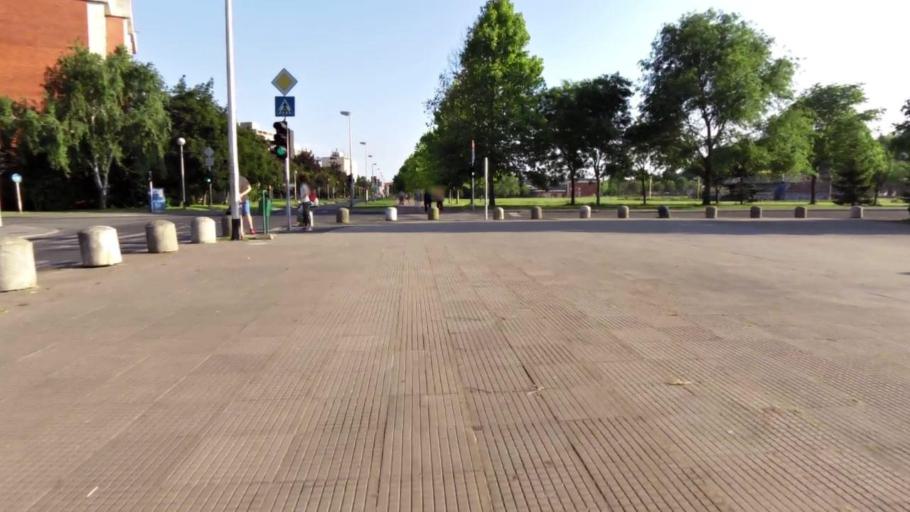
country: HR
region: Grad Zagreb
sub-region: Sesvete
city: Sesvete
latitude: 45.8327
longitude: 16.1072
